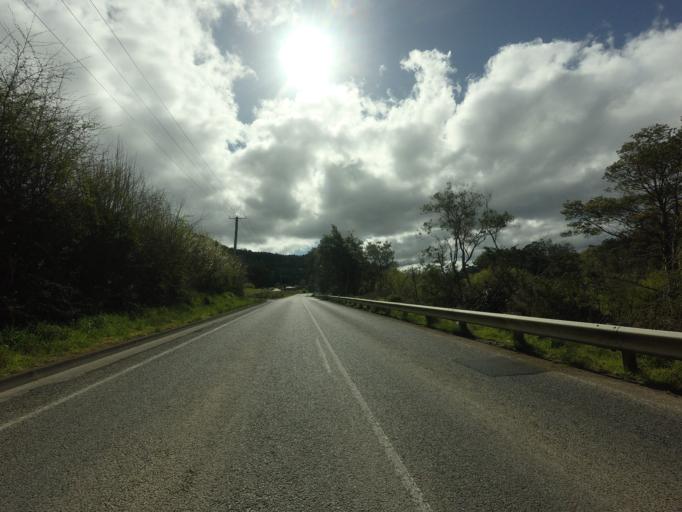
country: AU
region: Tasmania
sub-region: Huon Valley
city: Cygnet
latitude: -43.3060
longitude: 147.0095
